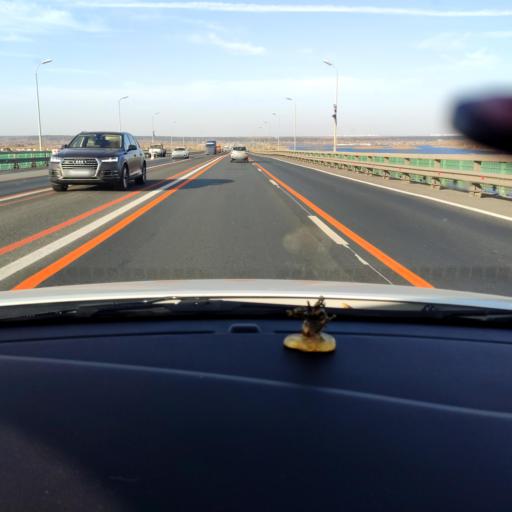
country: RU
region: Tatarstan
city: Osinovo
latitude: 55.7829
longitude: 48.8411
